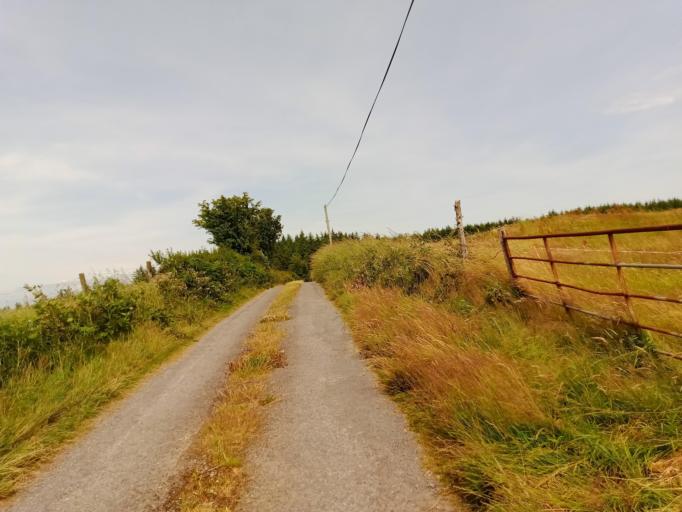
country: IE
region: Leinster
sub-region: Laois
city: Rathdowney
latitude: 52.7982
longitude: -7.4626
